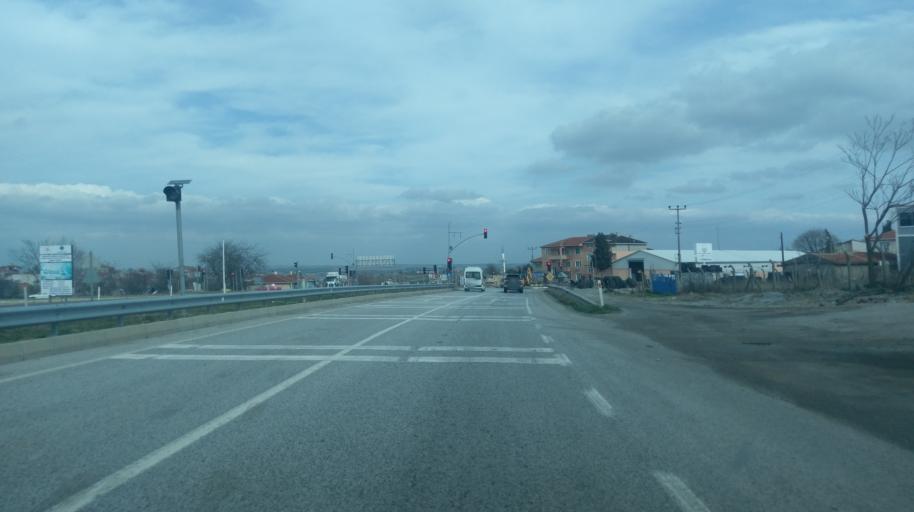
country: TR
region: Edirne
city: Kircasalih
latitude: 41.3906
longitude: 26.8005
